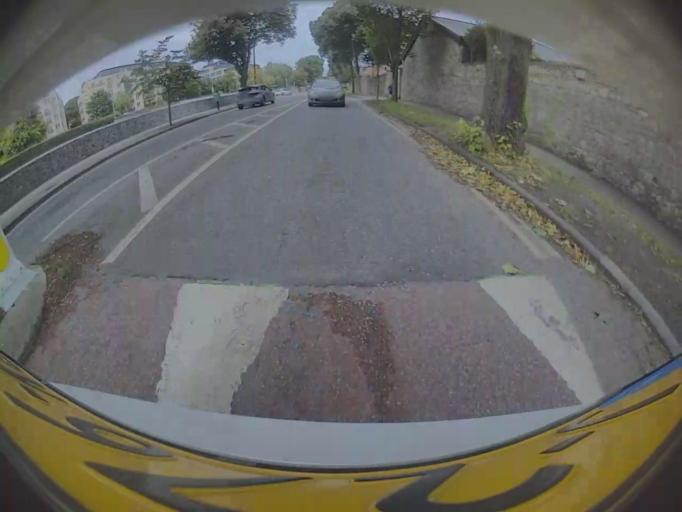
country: IE
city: Clonskeagh
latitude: 53.3266
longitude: -6.2310
